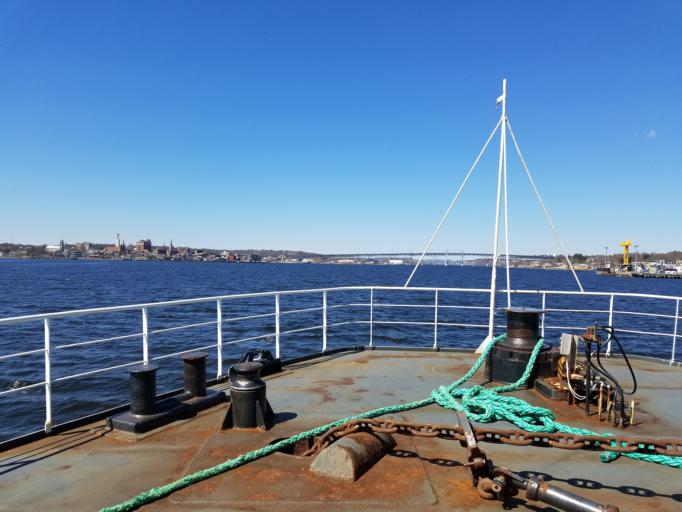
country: US
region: Connecticut
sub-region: New London County
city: New London
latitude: 41.3536
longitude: -72.0942
